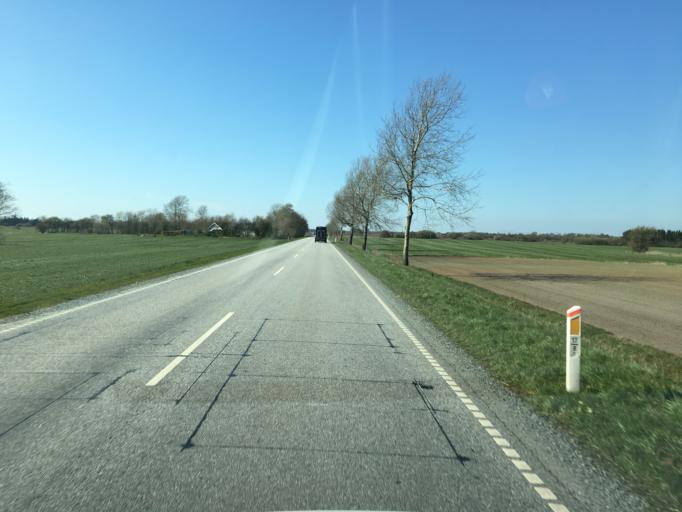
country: DK
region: South Denmark
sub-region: Aabenraa Kommune
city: Tinglev
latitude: 54.9575
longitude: 9.3338
